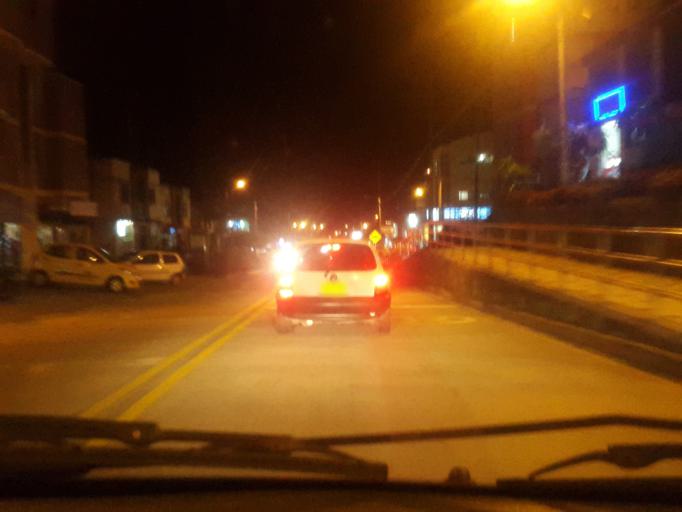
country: CO
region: Quindio
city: Armenia
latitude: 4.5211
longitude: -75.6970
